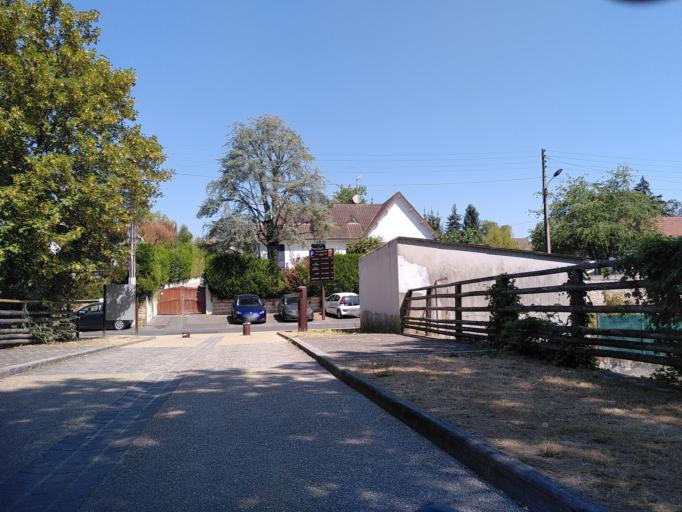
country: FR
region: Ile-de-France
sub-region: Departement de l'Essonne
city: Arpajon
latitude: 48.5908
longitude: 2.2410
